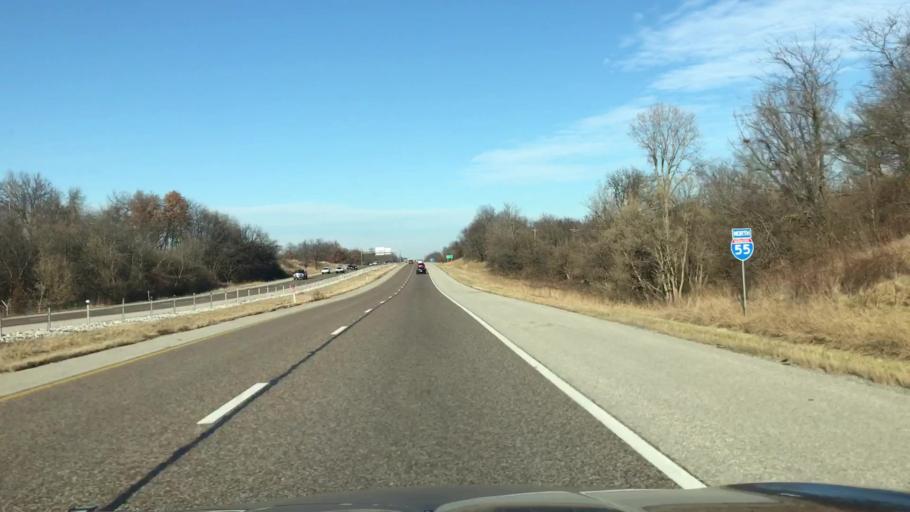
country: US
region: Illinois
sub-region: Madison County
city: Troy
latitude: 38.7646
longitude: -89.9036
